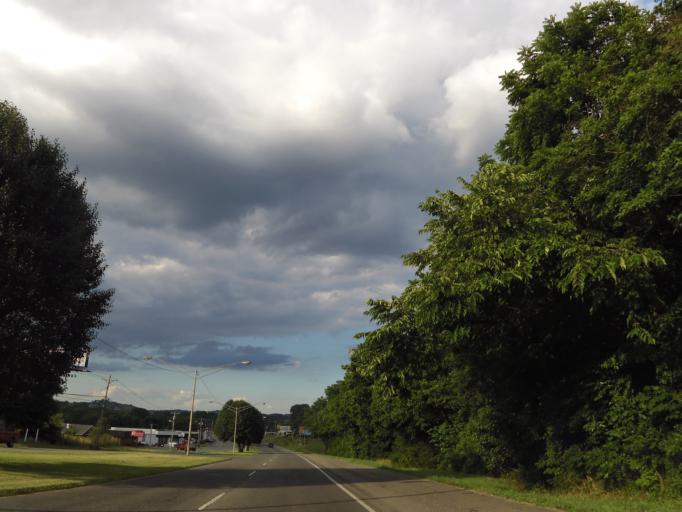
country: US
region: Tennessee
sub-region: Maury County
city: Columbia
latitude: 35.6313
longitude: -87.0227
